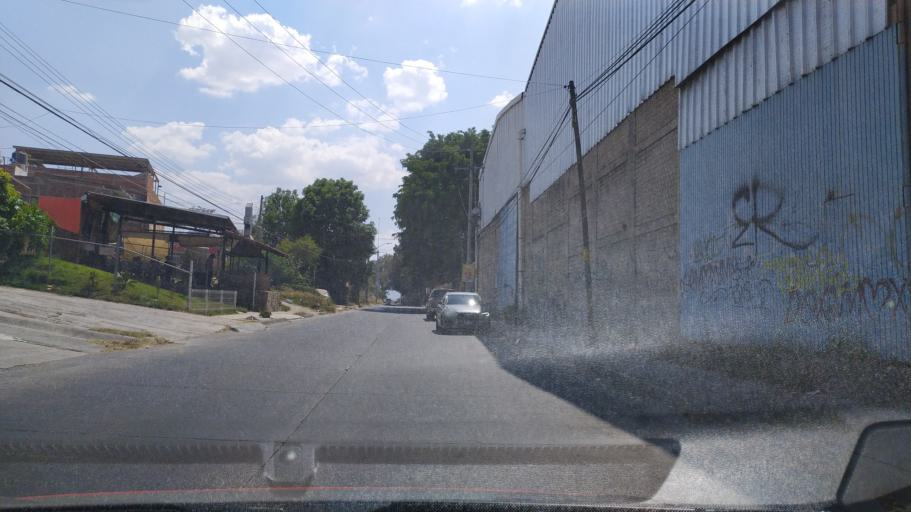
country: MX
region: Jalisco
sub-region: San Pedro Tlaquepaque
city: Paseo del Prado
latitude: 20.6152
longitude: -103.3928
